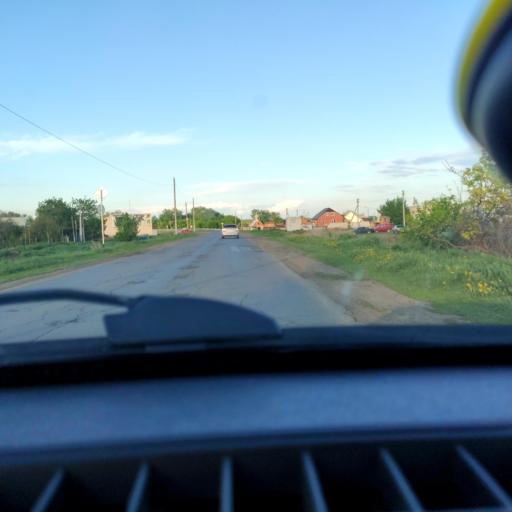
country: RU
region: Samara
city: Tol'yatti
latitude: 53.6813
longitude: 49.4249
